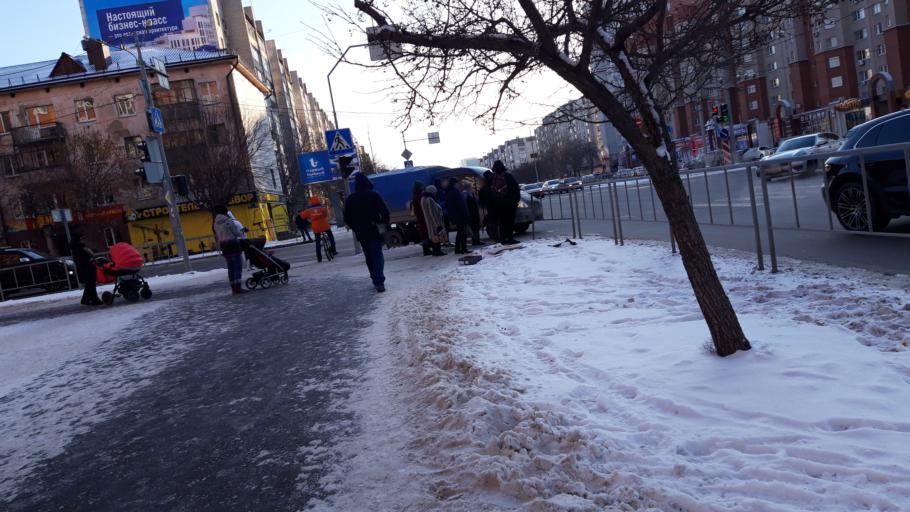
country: RU
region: Tjumen
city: Tyumen
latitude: 57.1528
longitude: 65.5682
